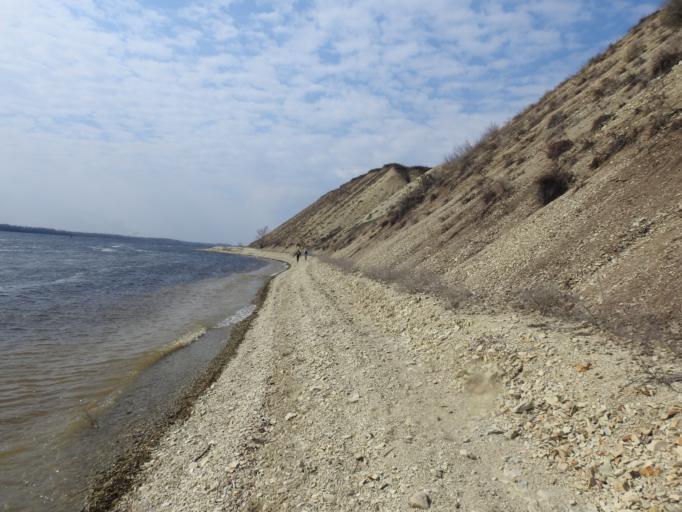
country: RU
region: Saratov
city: Voskresenskoye
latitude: 51.8030
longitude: 46.9077
